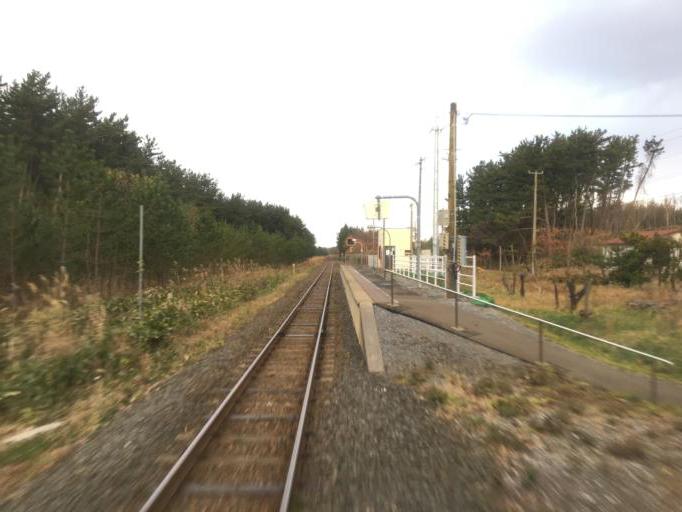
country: JP
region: Aomori
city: Mutsu
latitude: 41.2286
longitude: 141.2487
